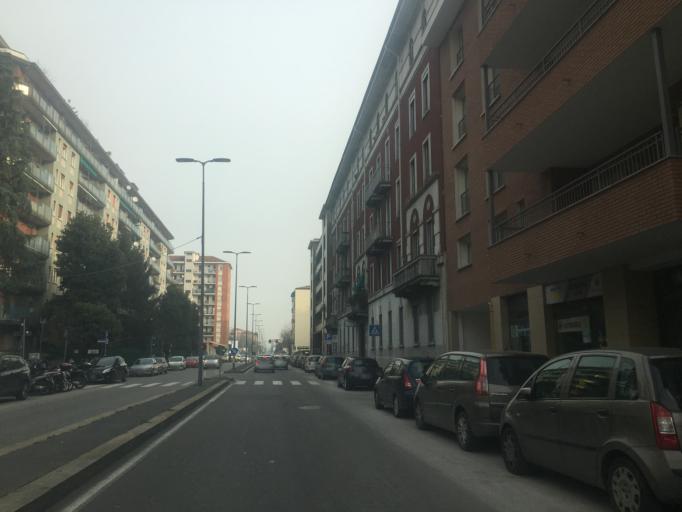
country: IT
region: Lombardy
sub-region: Citta metropolitana di Milano
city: Bresso
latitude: 45.5085
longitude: 9.2048
